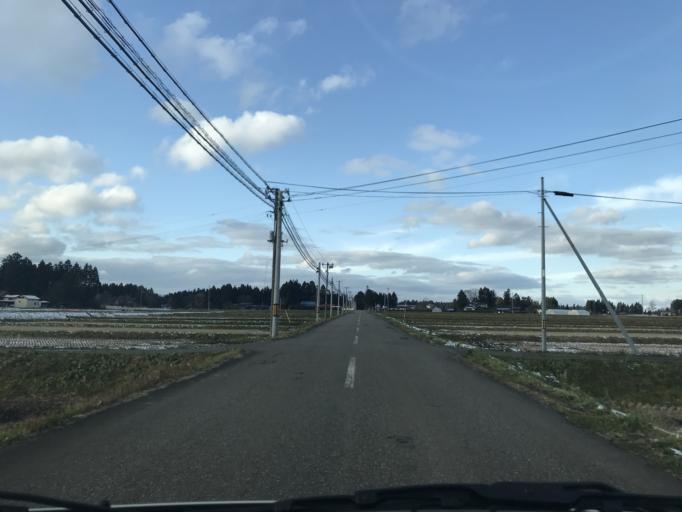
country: JP
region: Iwate
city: Kitakami
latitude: 39.2143
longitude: 141.0489
